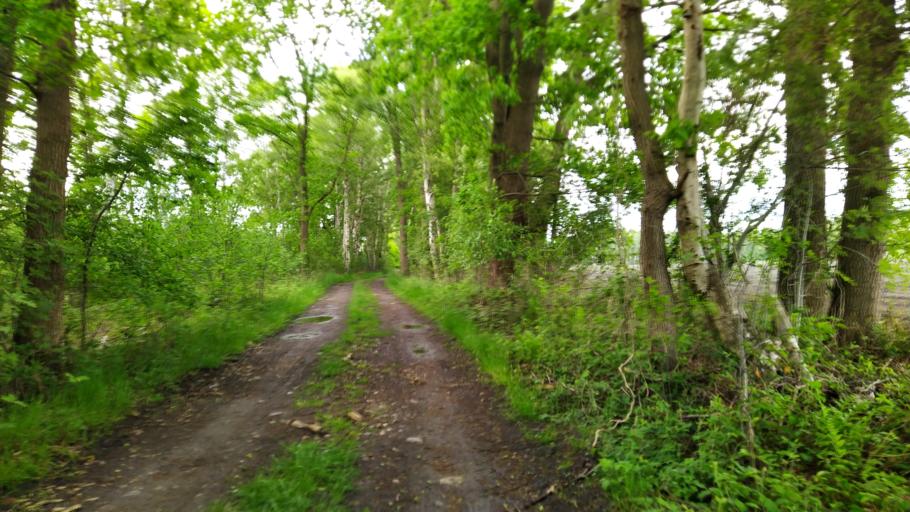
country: DE
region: Lower Saxony
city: Farven
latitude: 53.4176
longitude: 9.3469
